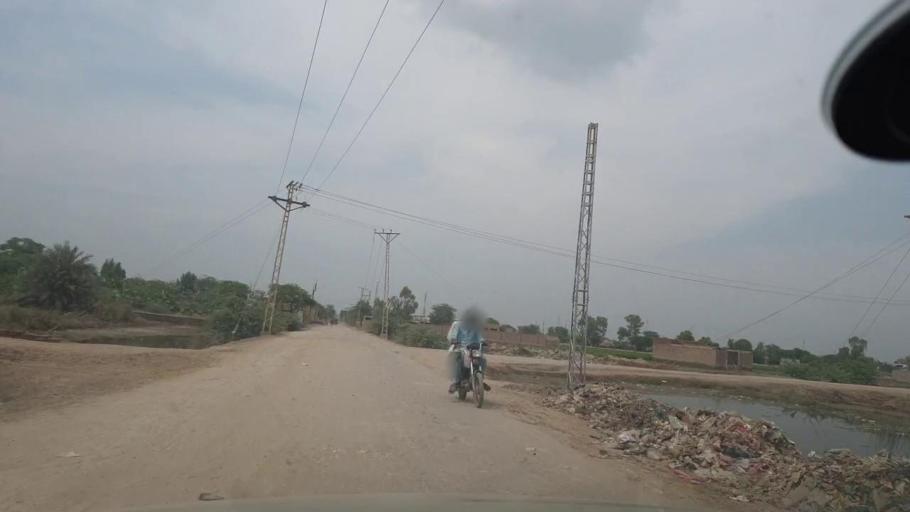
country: PK
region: Sindh
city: Jacobabad
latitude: 28.2623
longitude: 68.4375
